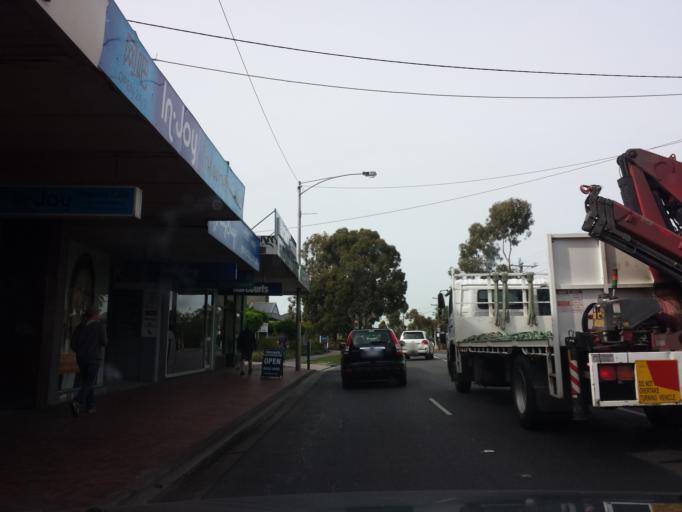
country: AU
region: Victoria
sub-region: Monash
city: Ashwood
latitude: -37.8785
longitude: 145.1285
